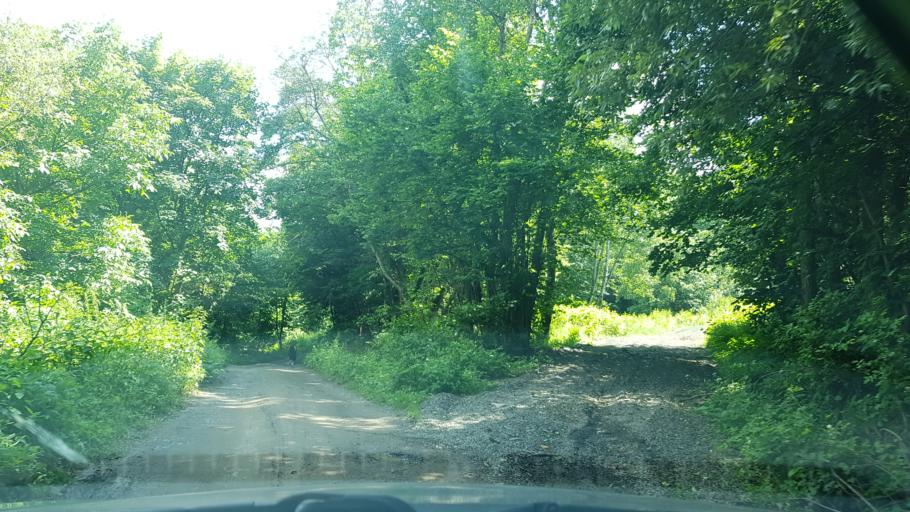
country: SK
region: Kosicky
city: Secovce
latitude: 48.5659
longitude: 21.4945
